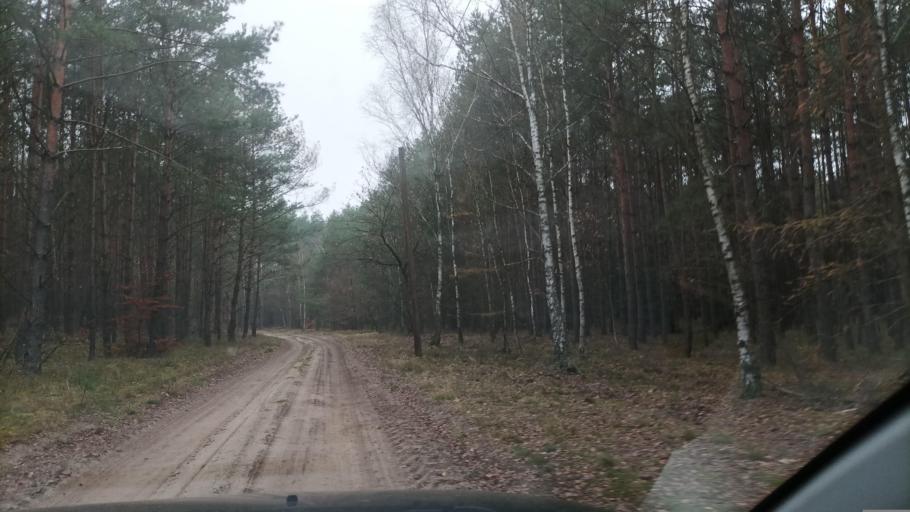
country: PL
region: Greater Poland Voivodeship
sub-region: Powiat czarnkowsko-trzcianecki
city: Polajewo
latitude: 52.7510
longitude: 16.7750
